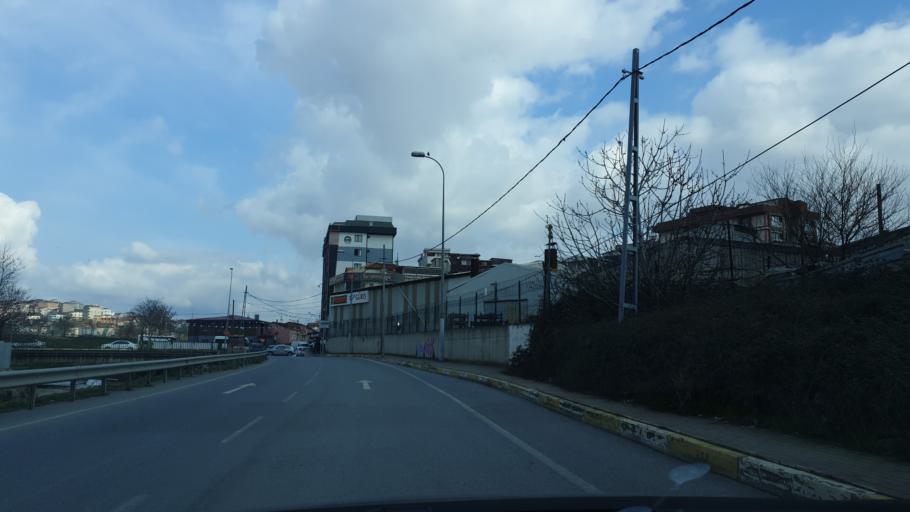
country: TR
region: Istanbul
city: Pendik
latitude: 40.8678
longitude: 29.2813
